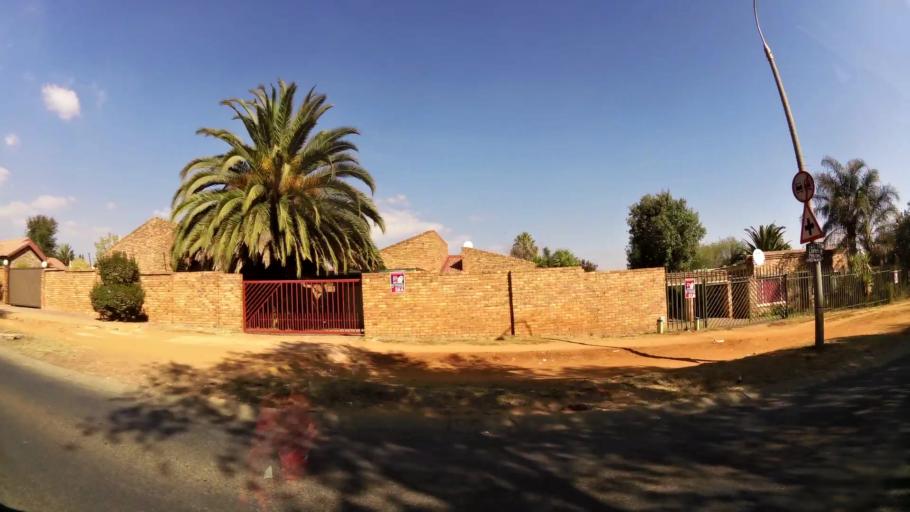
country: ZA
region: Gauteng
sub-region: Ekurhuleni Metropolitan Municipality
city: Tembisa
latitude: -26.0681
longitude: 28.2426
